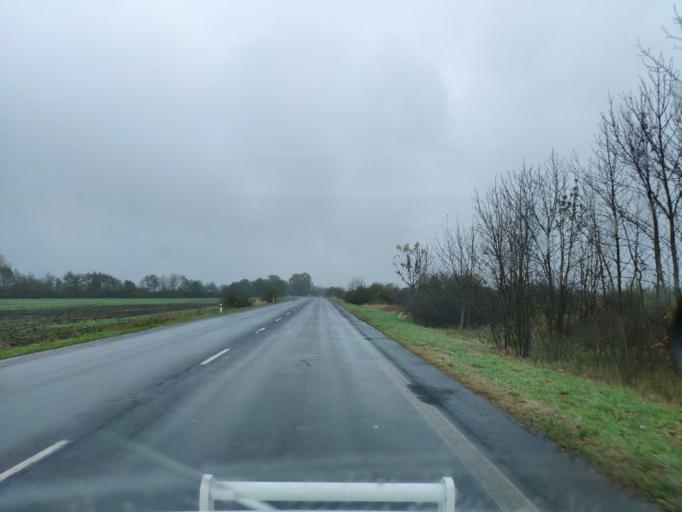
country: SK
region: Kosicky
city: Cierna nad Tisou
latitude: 48.4279
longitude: 21.9915
